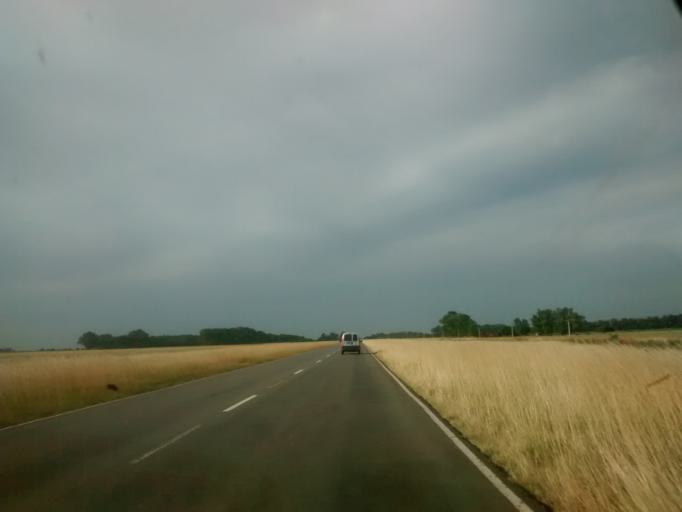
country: AR
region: Buenos Aires
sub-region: Partido de Ayacucho
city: Ayacucho
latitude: -36.6694
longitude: -58.5745
